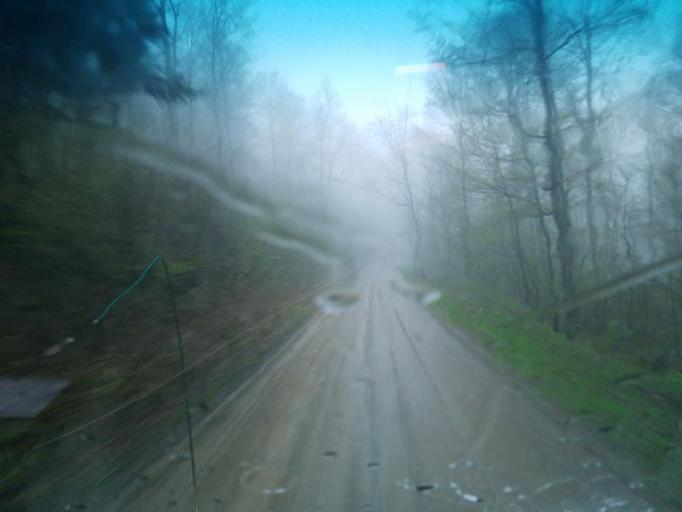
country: US
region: Pennsylvania
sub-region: Tioga County
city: Westfield
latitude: 41.9327
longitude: -77.7084
